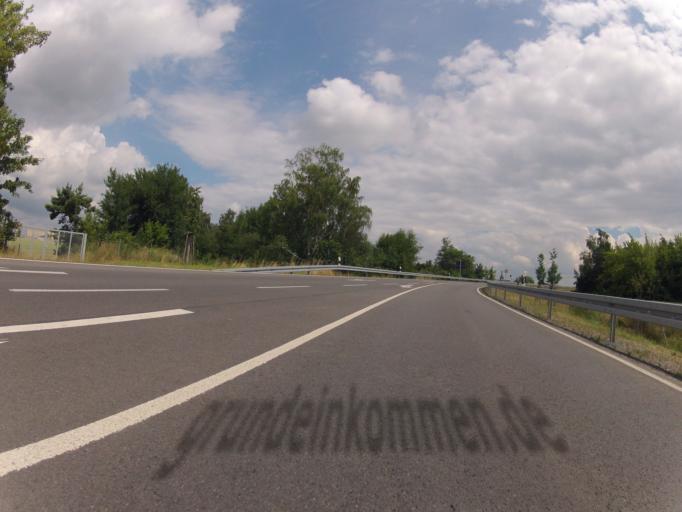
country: DE
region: Saxony
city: Wurzen
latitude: 51.3799
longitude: 12.7720
